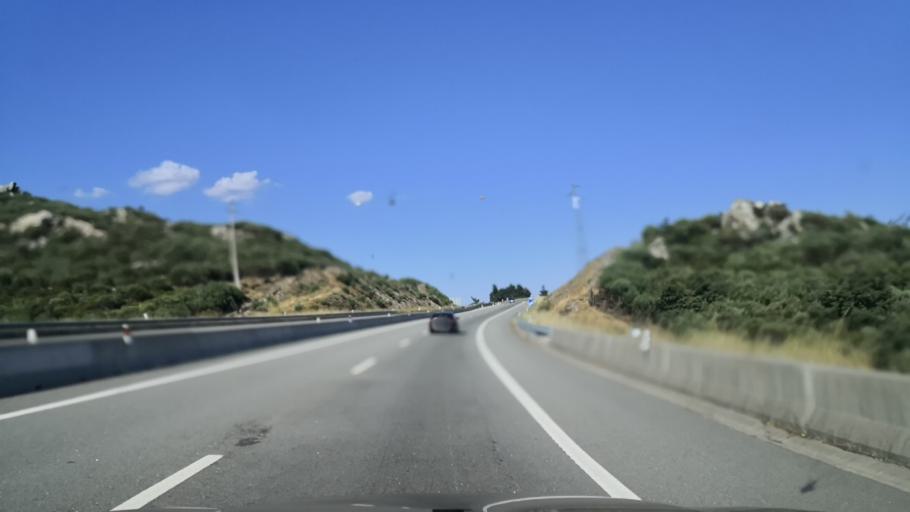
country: PT
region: Vila Real
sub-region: Murca
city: Murca
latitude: 41.3768
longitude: -7.5232
